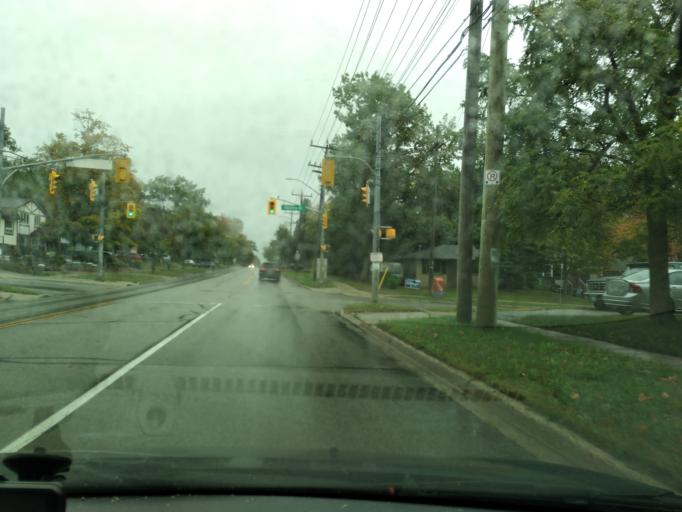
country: CA
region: Ontario
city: Barrie
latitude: 44.4072
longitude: -79.6986
